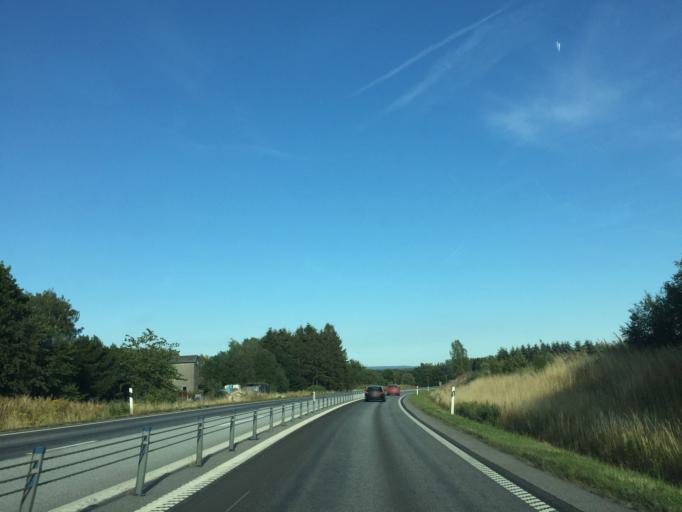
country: SE
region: Skane
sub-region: Lunds Kommun
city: Genarp
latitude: 55.6560
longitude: 13.4177
